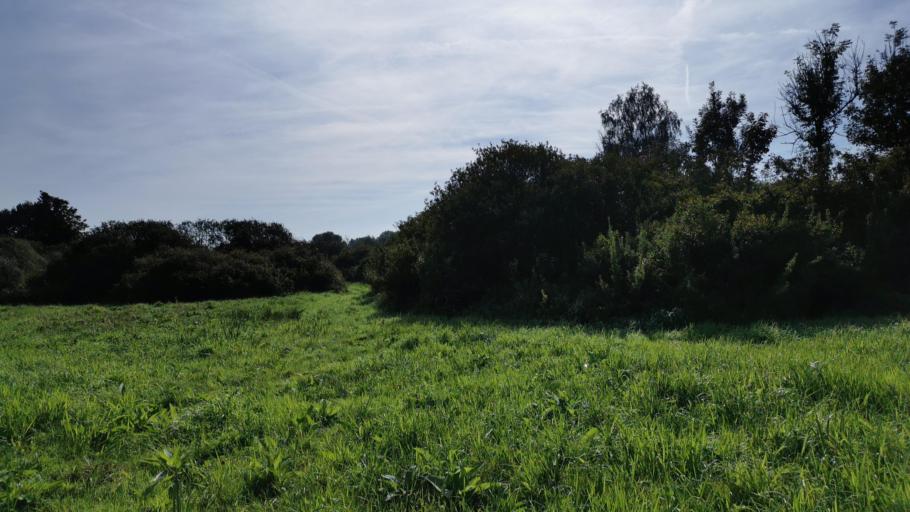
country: FR
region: Picardie
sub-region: Departement de la Somme
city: Longpre-les-Corps-Saints
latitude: 50.0401
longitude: 1.9596
